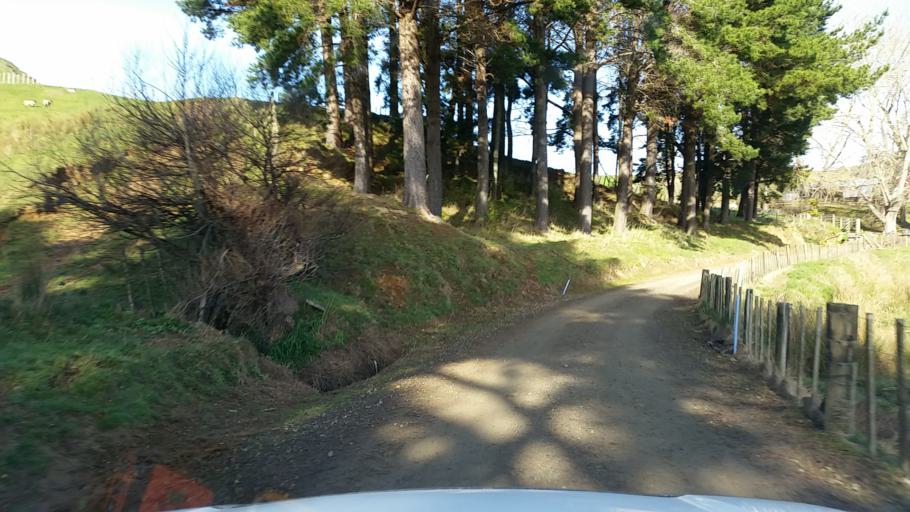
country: NZ
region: Taranaki
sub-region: South Taranaki District
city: Eltham
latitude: -39.3182
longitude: 174.5327
